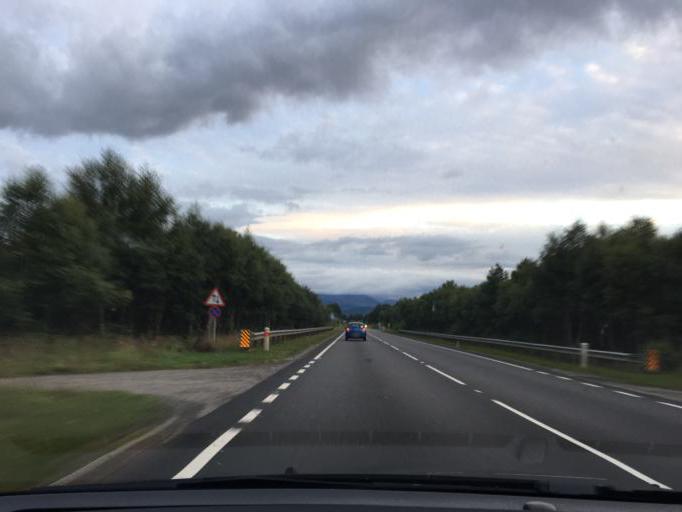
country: GB
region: Scotland
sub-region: Highland
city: Aviemore
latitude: 57.2439
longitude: -3.8072
